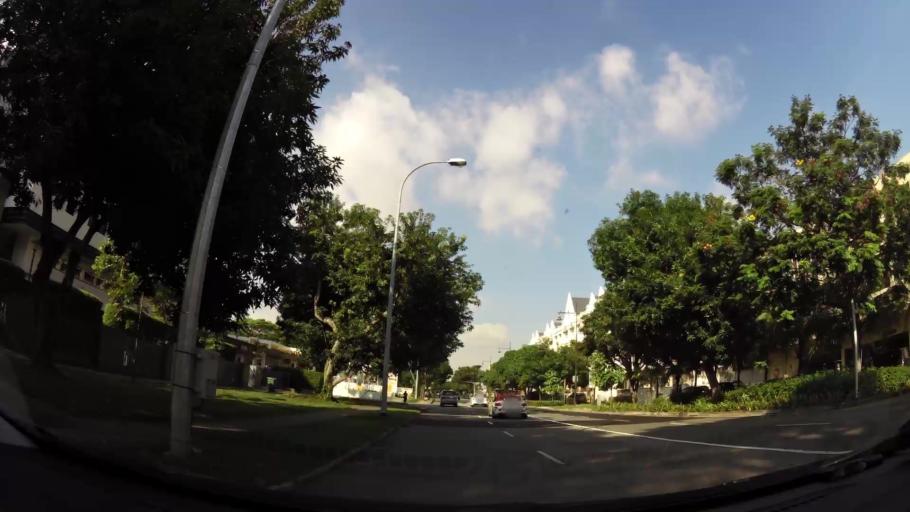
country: SG
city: Singapore
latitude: 1.3129
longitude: 103.9271
